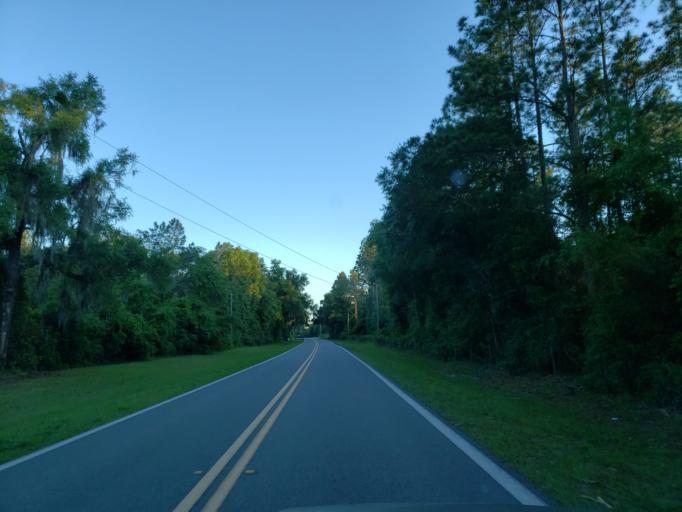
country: US
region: Georgia
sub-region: Lowndes County
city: Valdosta
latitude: 30.6242
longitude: -83.2566
